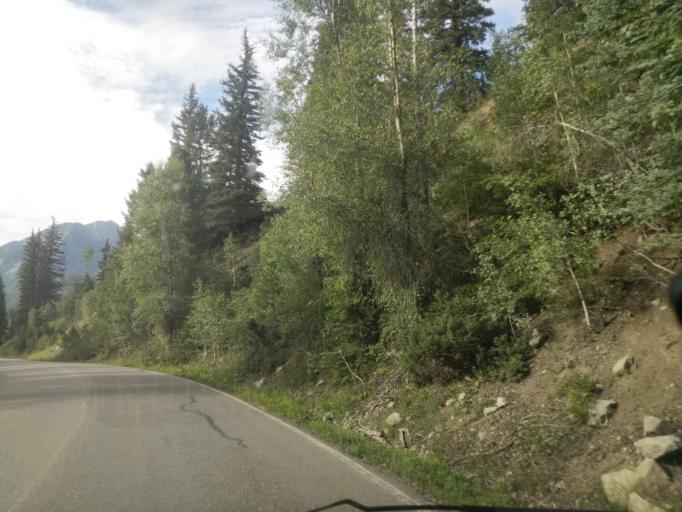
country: US
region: Colorado
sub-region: Garfield County
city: Carbondale
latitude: 39.1057
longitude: -107.2652
